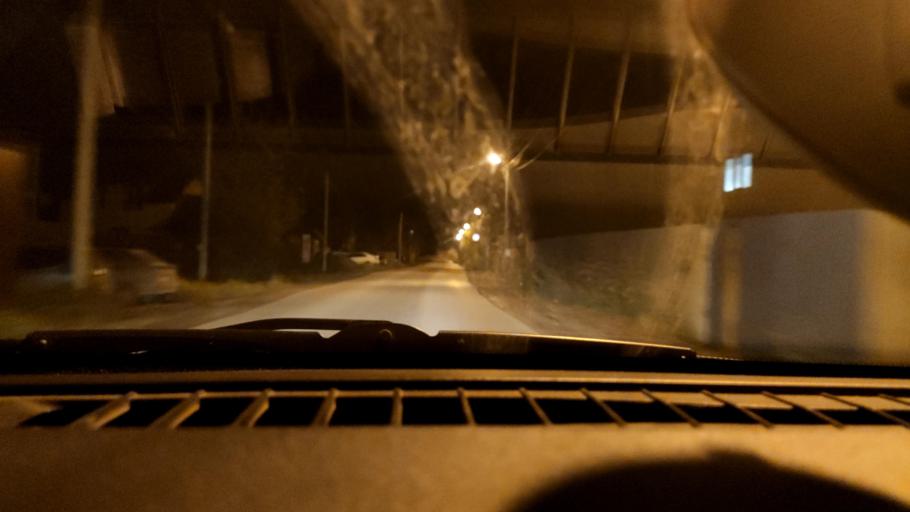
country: RU
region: Perm
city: Ferma
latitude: 57.9037
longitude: 56.3043
